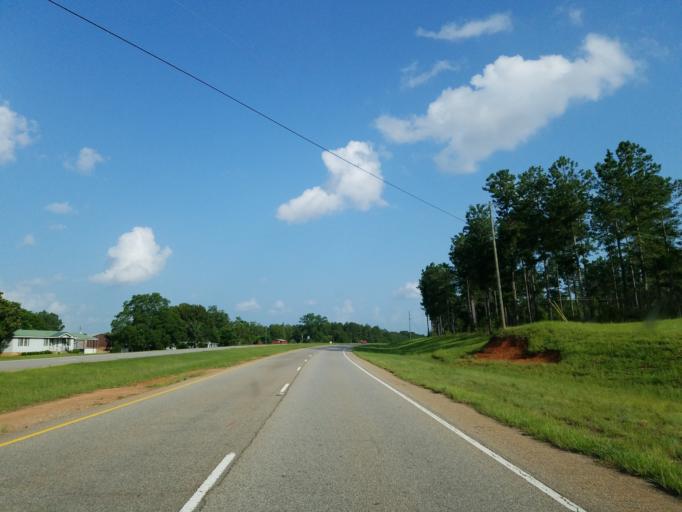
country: US
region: Georgia
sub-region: Pulaski County
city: Hawkinsville
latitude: 32.3387
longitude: -83.5674
